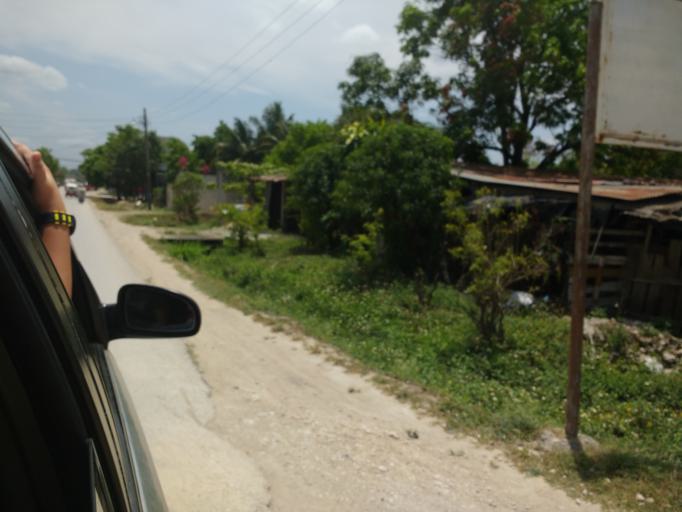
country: GT
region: Peten
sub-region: Municipio de San Benito
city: San Benito
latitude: 16.9194
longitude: -89.9113
